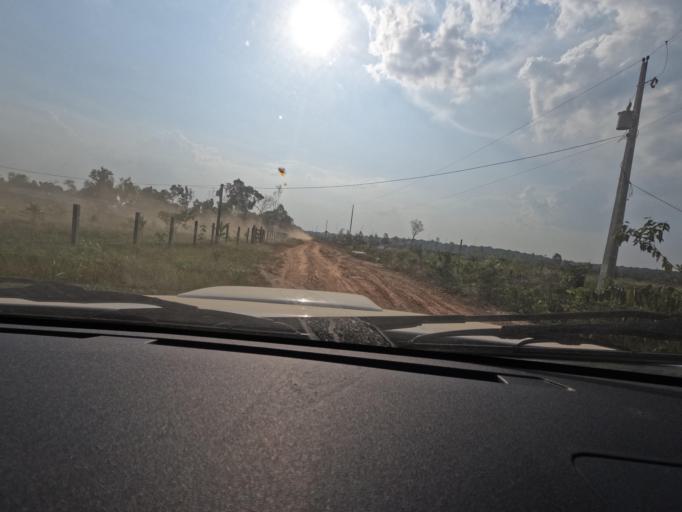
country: BR
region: Rondonia
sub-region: Porto Velho
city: Porto Velho
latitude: -8.5730
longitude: -64.0161
